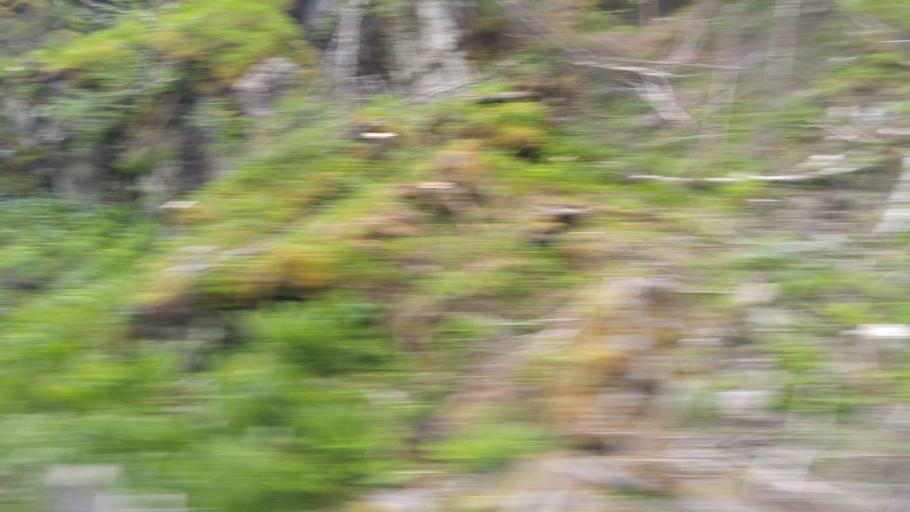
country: NO
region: Nord-Trondelag
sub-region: Meraker
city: Meraker
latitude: 63.4657
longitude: 11.4817
